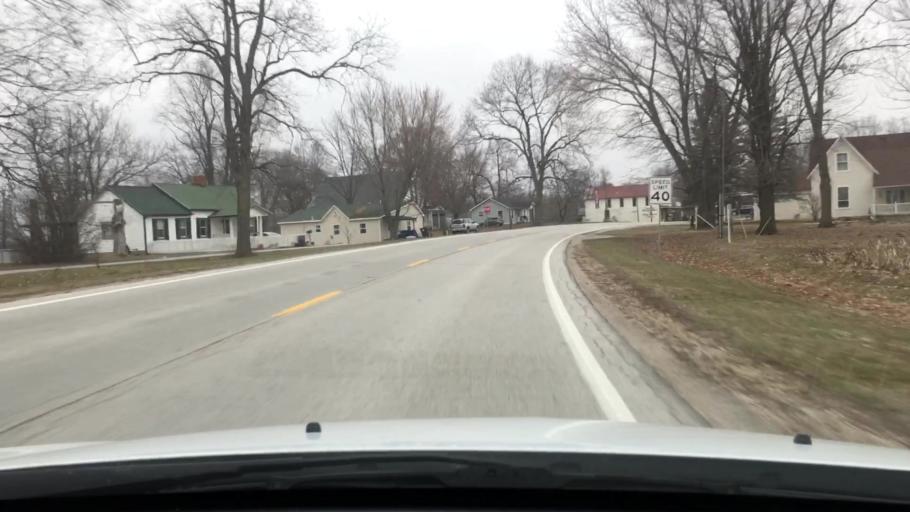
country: US
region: Illinois
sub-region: Pike County
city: Pittsfield
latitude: 39.5447
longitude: -90.9203
